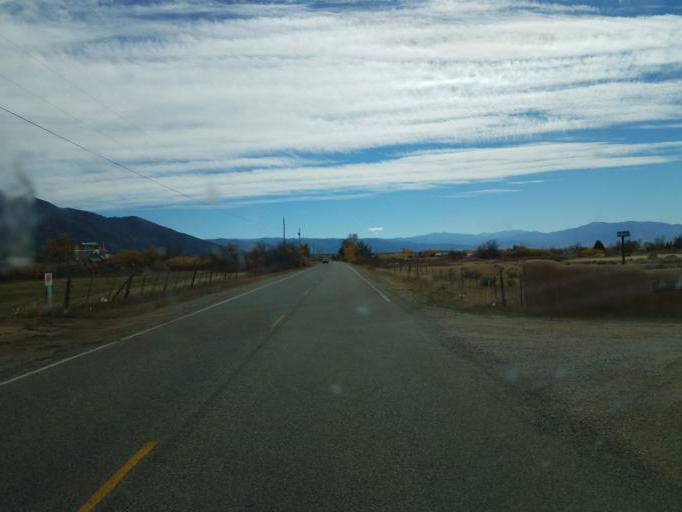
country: US
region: New Mexico
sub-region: Taos County
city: Arroyo Seco
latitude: 36.5288
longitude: -105.5718
